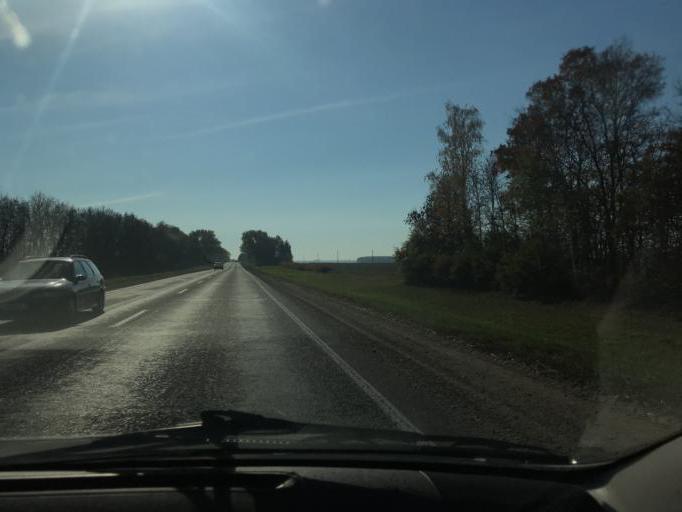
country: BY
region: Minsk
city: Salihorsk
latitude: 52.8439
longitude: 27.4663
